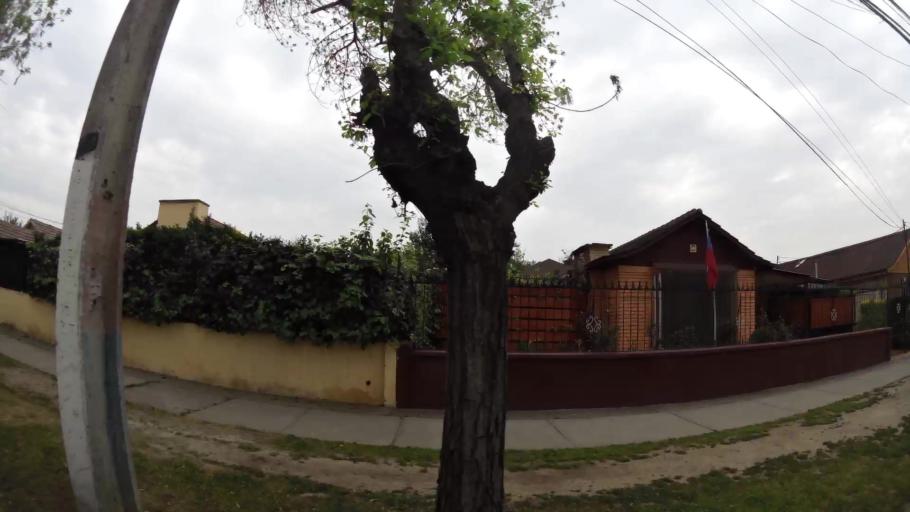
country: CL
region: Santiago Metropolitan
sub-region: Provincia de Santiago
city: Villa Presidente Frei, Nunoa, Santiago, Chile
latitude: -33.4922
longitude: -70.5909
